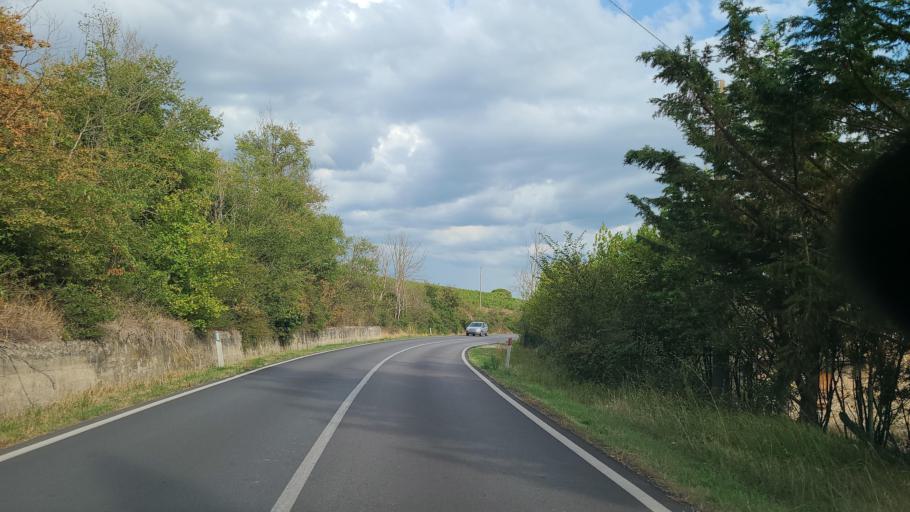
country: IT
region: Tuscany
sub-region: Provincia di Siena
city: San Gimignano
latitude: 43.4832
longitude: 11.0063
